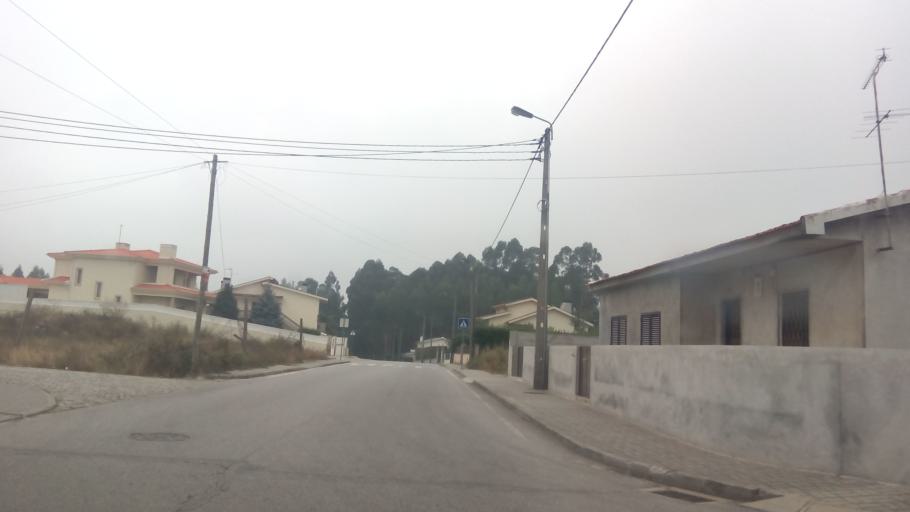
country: PT
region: Porto
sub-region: Paredes
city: Rebordosa
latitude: 41.2165
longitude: -8.3795
